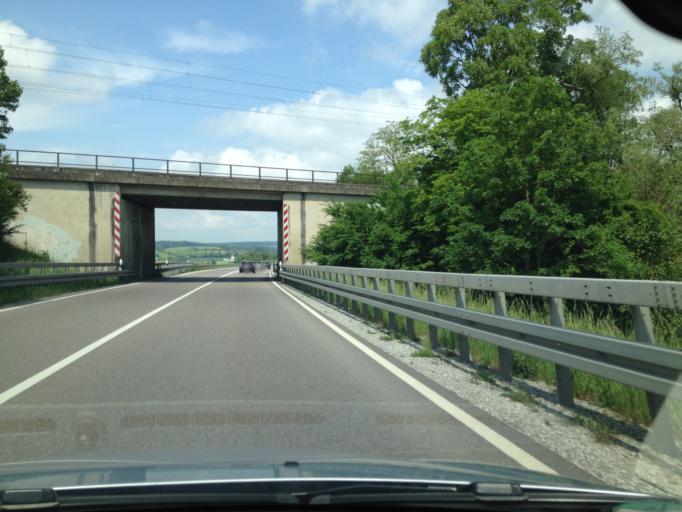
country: DE
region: Bavaria
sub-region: Swabia
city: Donauwoerth
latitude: 48.7419
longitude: 10.7382
